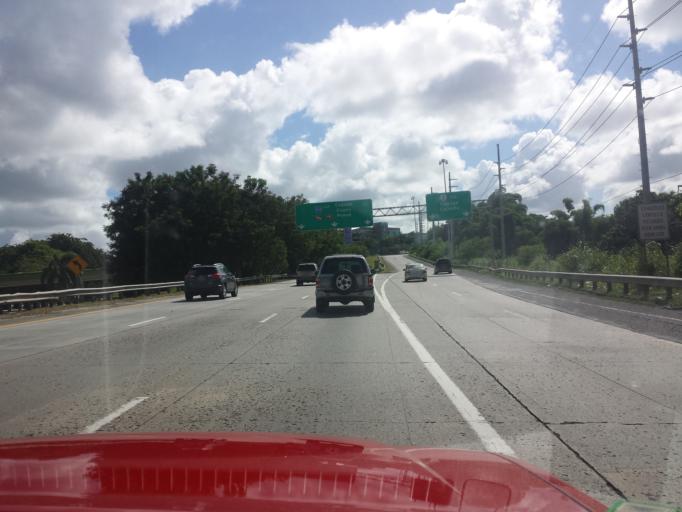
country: PR
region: Guaynabo
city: Guaynabo
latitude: 18.3795
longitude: -66.0716
